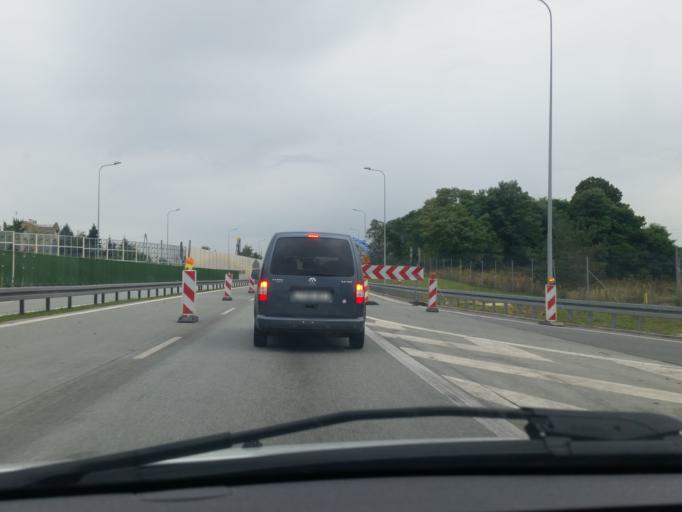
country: PL
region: Lodz Voivodeship
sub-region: Powiat skierniewicki
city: Kowiesy
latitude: 51.9186
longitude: 20.4550
